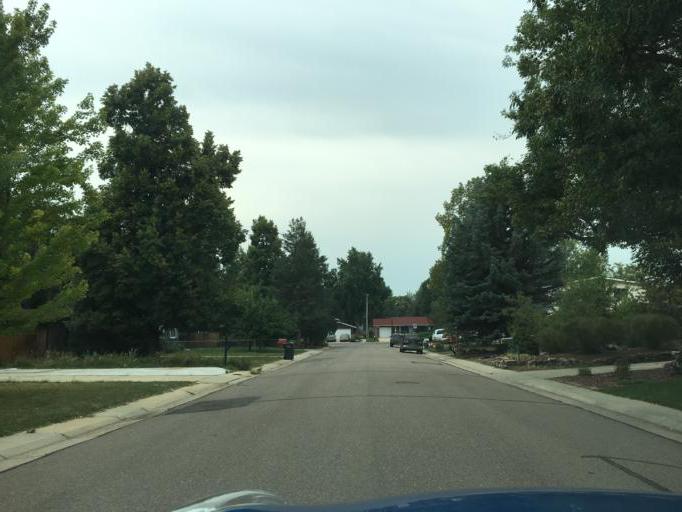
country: US
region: Colorado
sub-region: Jefferson County
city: Wheat Ridge
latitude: 39.7540
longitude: -105.0915
